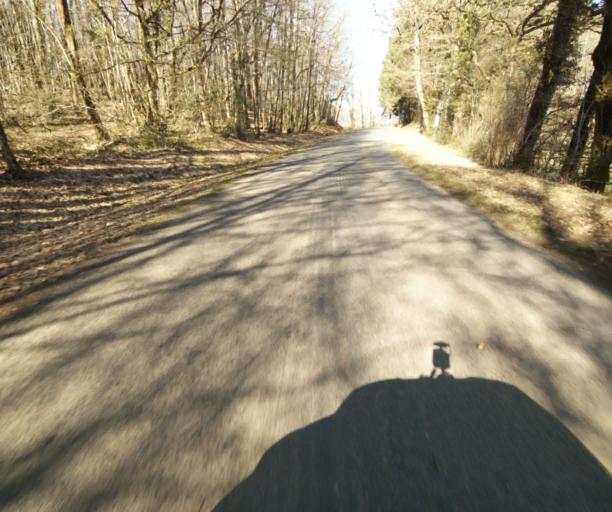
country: FR
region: Limousin
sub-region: Departement de la Correze
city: Seilhac
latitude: 45.3988
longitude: 1.7502
